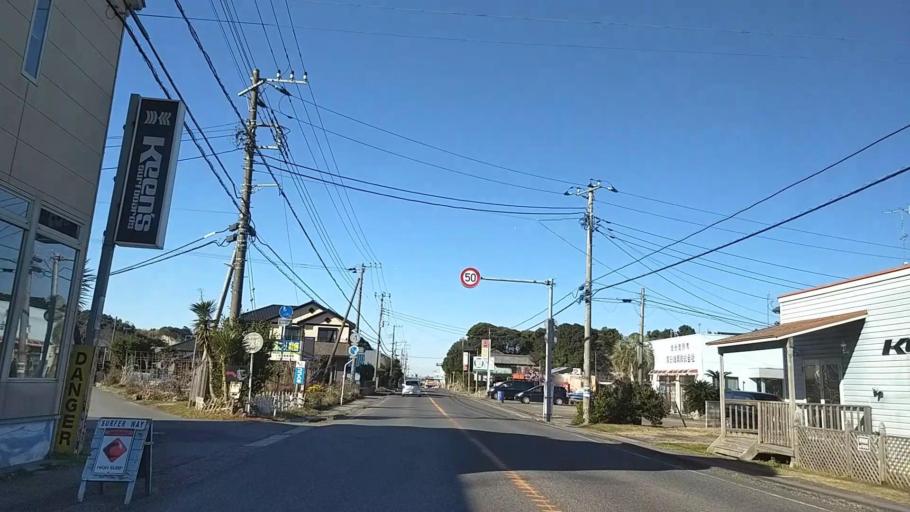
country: JP
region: Chiba
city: Ohara
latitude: 35.3277
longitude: 140.3980
